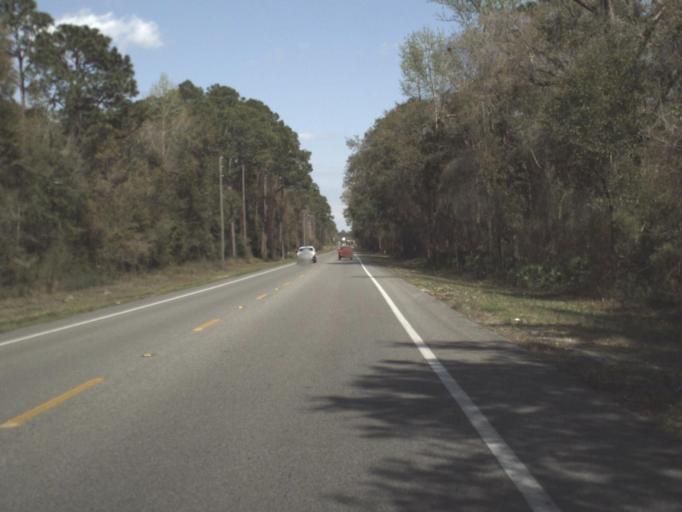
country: US
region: Florida
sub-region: Wakulla County
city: Crawfordville
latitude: 30.0780
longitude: -84.4021
